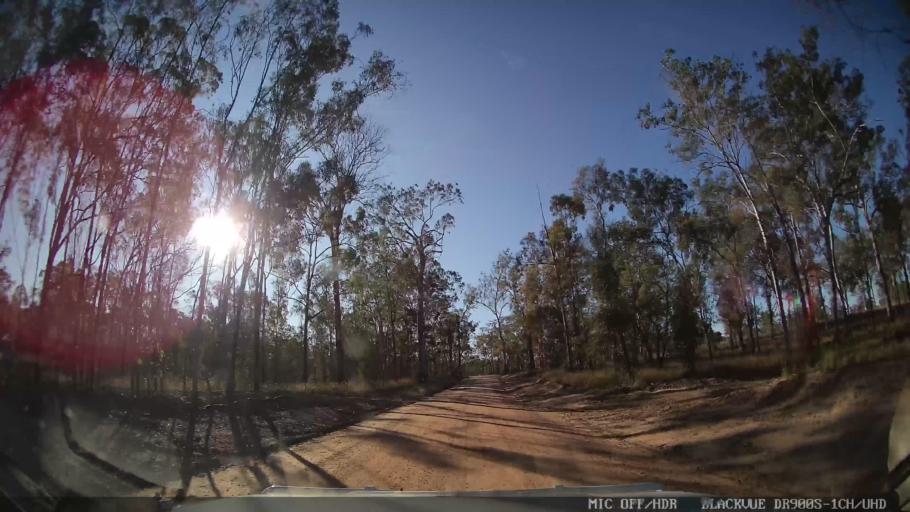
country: AU
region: Queensland
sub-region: Bundaberg
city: Sharon
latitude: -24.7377
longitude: 151.5234
